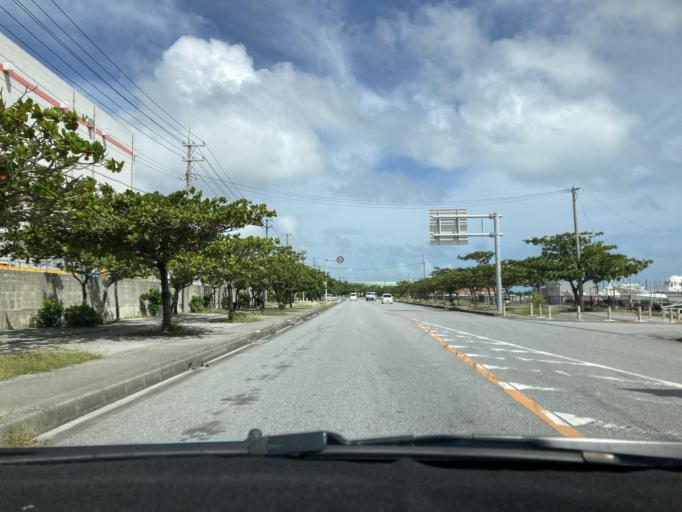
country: JP
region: Okinawa
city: Ginowan
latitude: 26.2173
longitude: 127.7763
